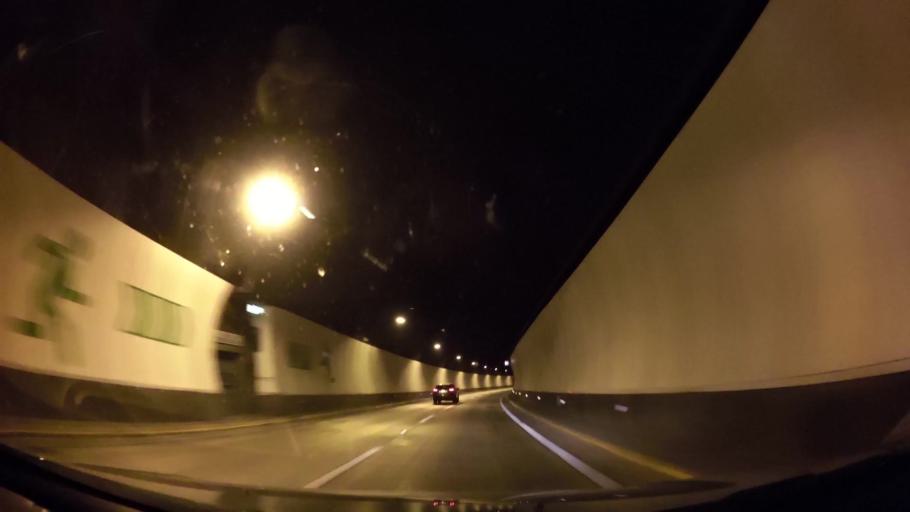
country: CL
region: Santiago Metropolitan
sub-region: Provincia de Santiago
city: Santiago
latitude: -33.4081
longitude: -70.6149
